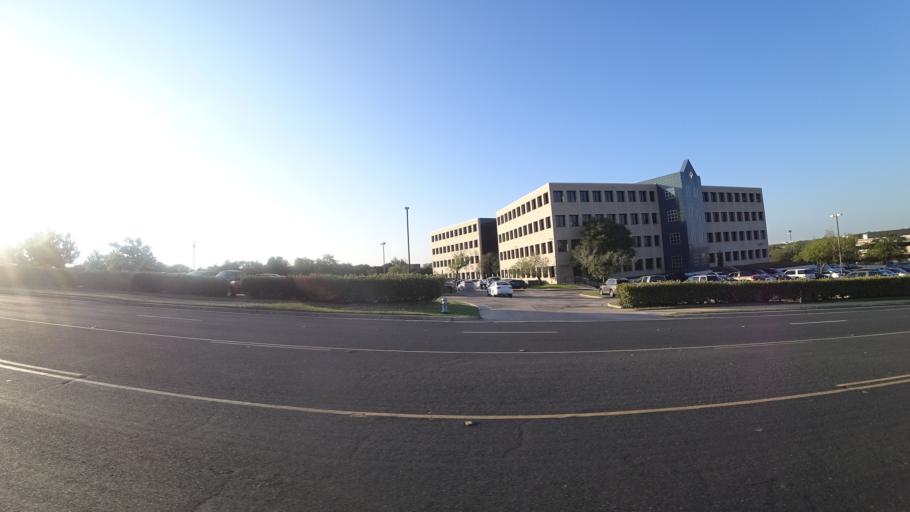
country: US
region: Texas
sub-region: Travis County
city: Austin
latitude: 30.3383
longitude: -97.6753
